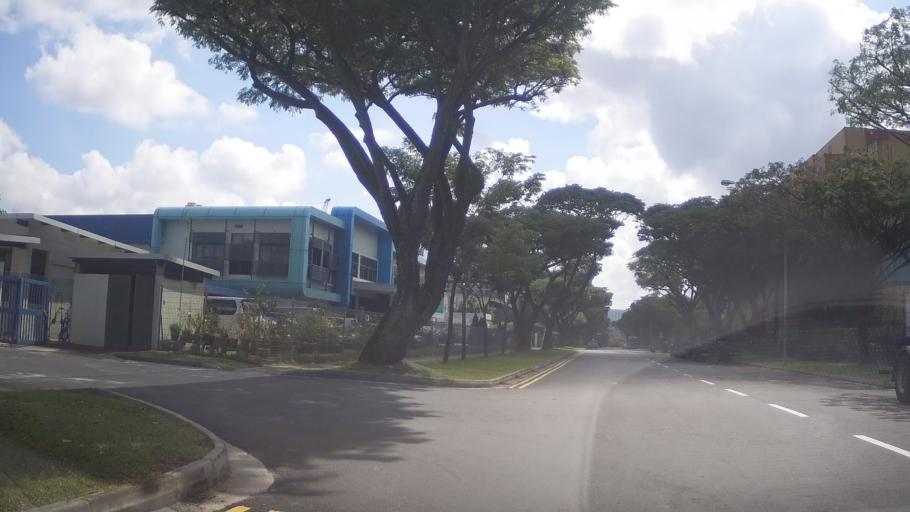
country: MY
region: Johor
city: Johor Bahru
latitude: 1.3122
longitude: 103.6730
